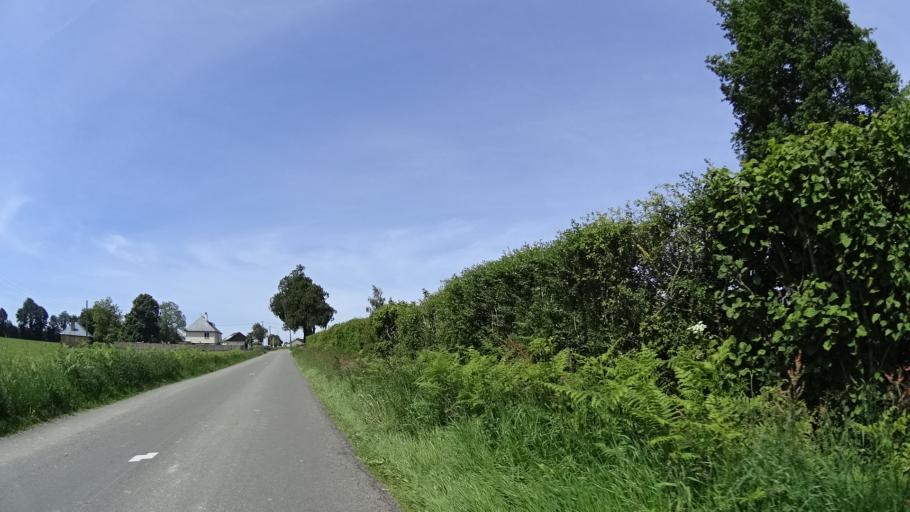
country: FR
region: Brittany
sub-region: Departement d'Ille-et-Vilaine
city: Saint-Gilles
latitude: 48.1952
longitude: -1.8445
